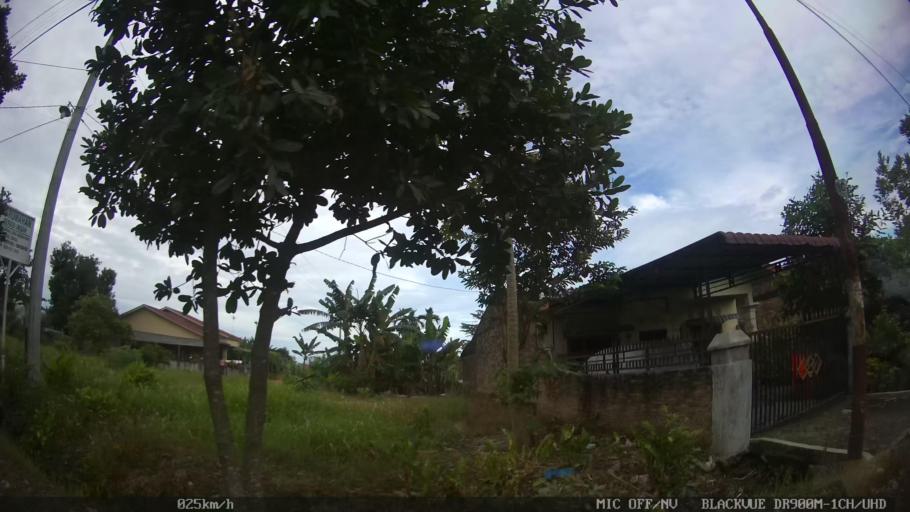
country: ID
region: North Sumatra
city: Sunggal
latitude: 3.5814
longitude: 98.5650
